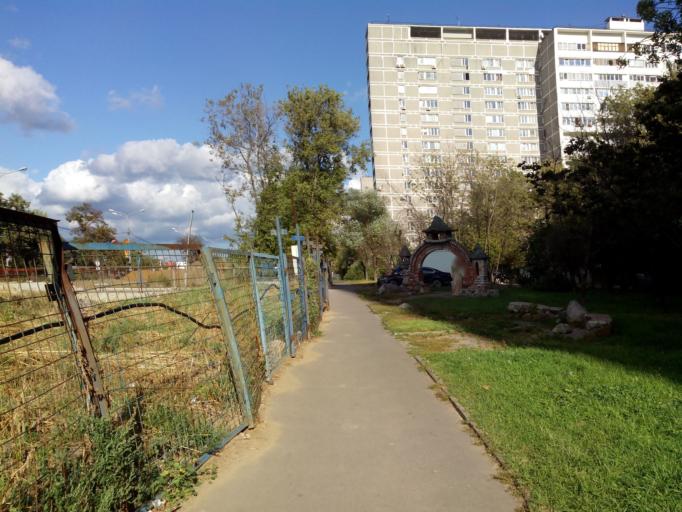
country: RU
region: Moskovskaya
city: Bogorodskoye
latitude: 55.7992
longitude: 37.7360
